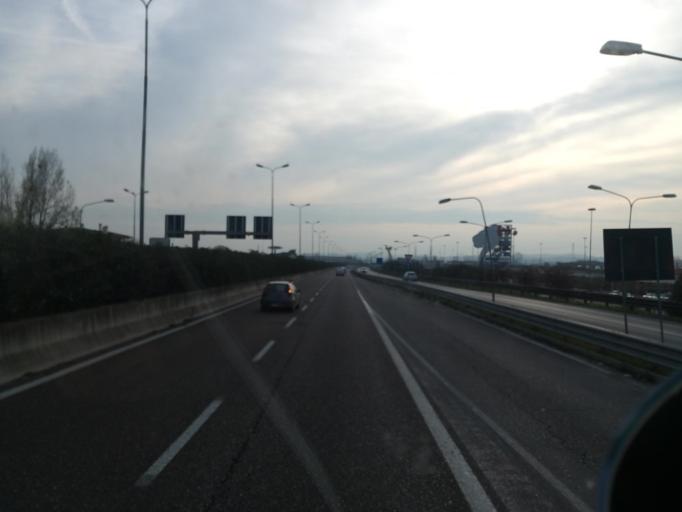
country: IT
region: Lombardy
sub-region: Provincia di Brescia
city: Desenzano del Garda
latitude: 45.4318
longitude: 10.5171
